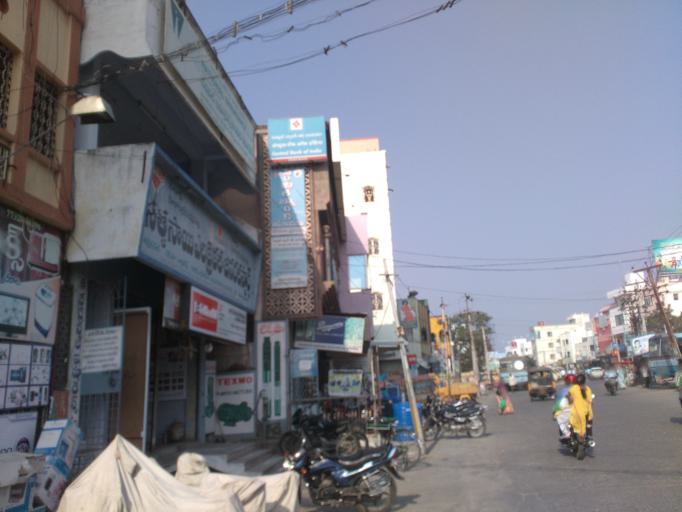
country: IN
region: Andhra Pradesh
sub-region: Prakasam
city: Chirala
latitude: 15.8287
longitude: 80.3571
